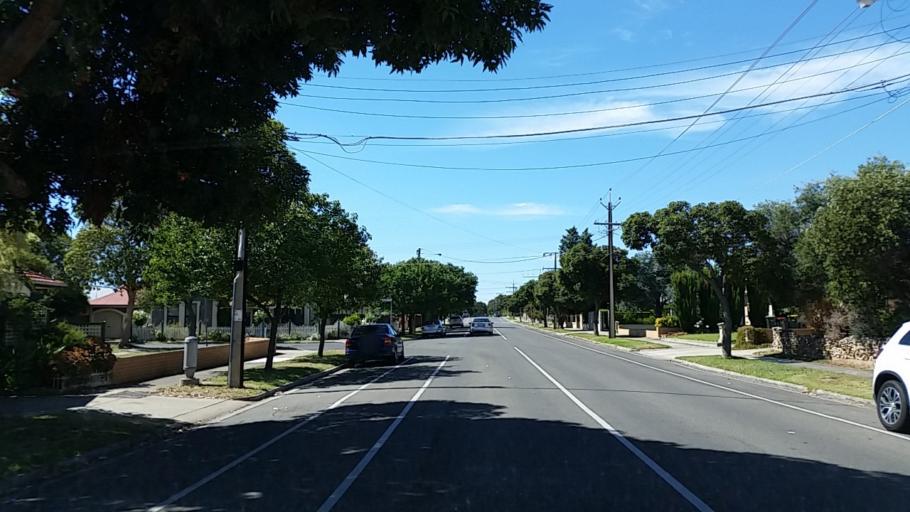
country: AU
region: South Australia
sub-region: Charles Sturt
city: Findon
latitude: -34.9223
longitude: 138.5288
